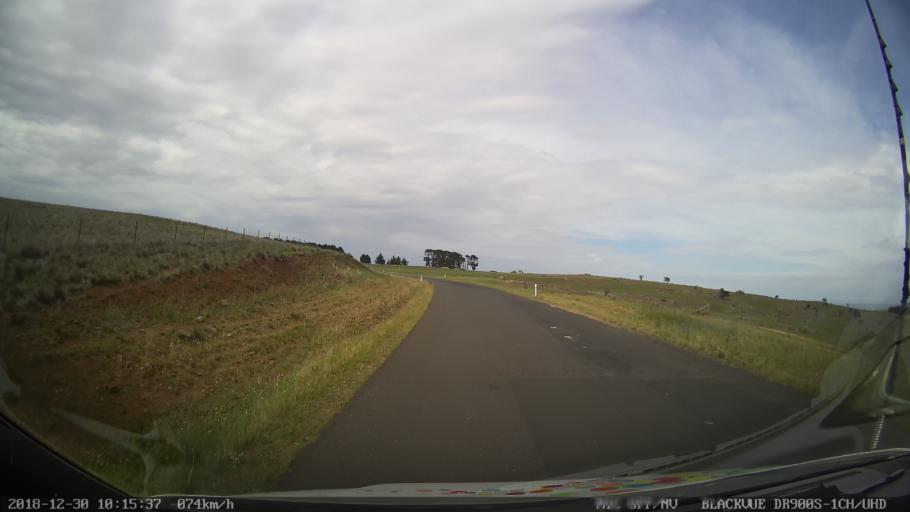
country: AU
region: New South Wales
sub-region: Snowy River
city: Berridale
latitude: -36.5439
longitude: 149.0442
